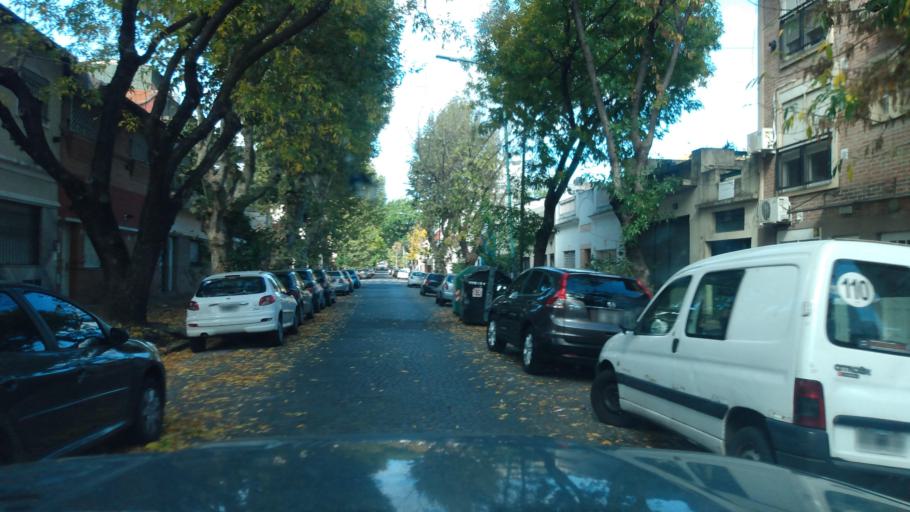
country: AR
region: Buenos Aires
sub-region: Partido de General San Martin
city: General San Martin
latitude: -34.5699
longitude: -58.4949
